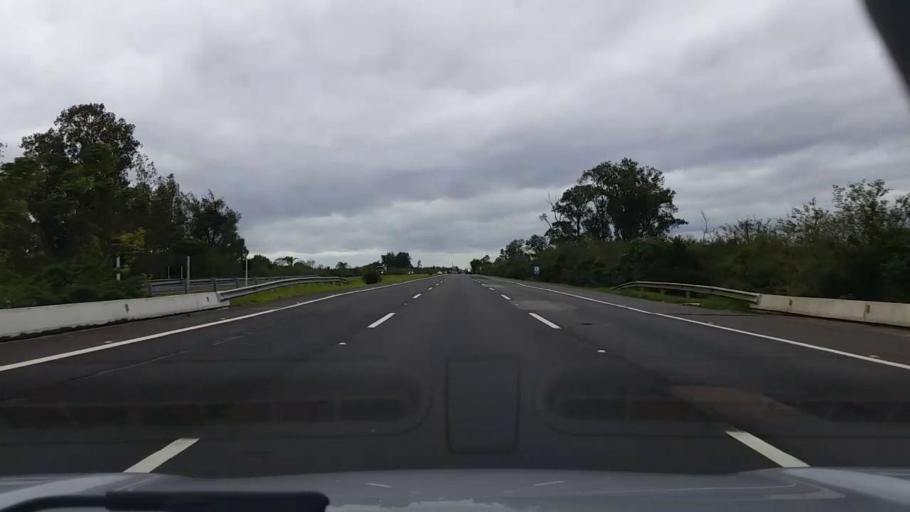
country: BR
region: Rio Grande do Sul
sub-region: Rolante
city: Rolante
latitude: -29.8835
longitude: -50.5505
